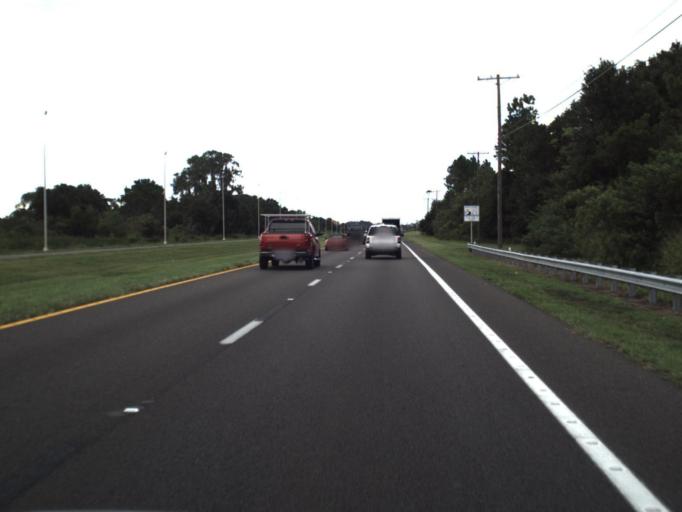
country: US
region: Florida
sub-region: Polk County
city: Fuller Heights
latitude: 27.9247
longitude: -81.9739
